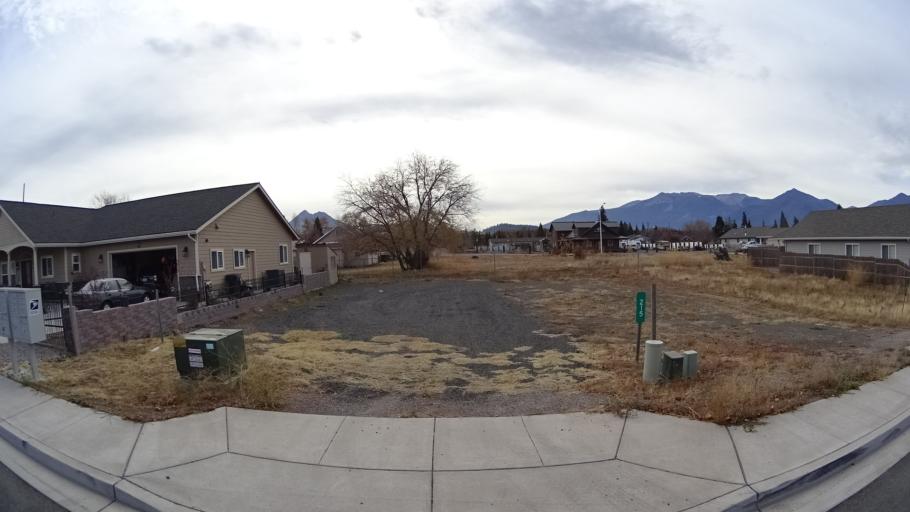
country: US
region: California
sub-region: Siskiyou County
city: Weed
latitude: 41.4377
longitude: -122.3801
